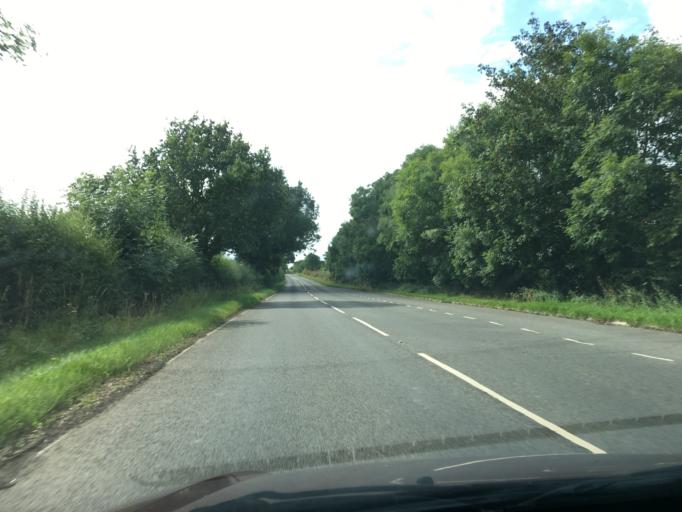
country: GB
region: England
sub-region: Warwickshire
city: Royal Leamington Spa
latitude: 52.3255
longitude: -1.5258
